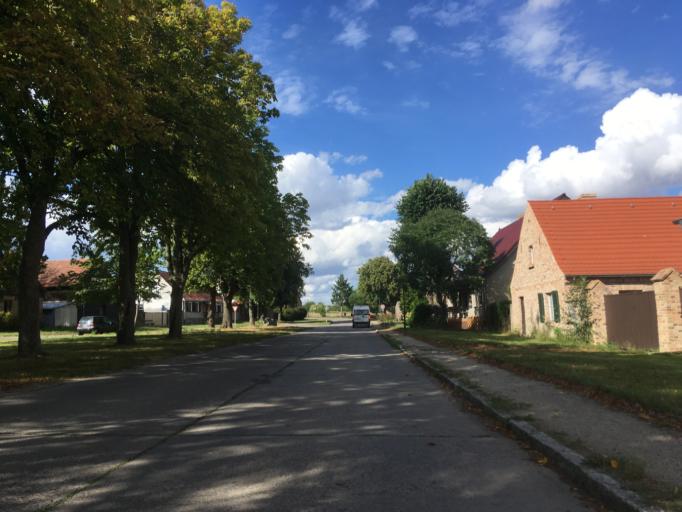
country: DE
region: Brandenburg
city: Liepe
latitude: 52.9137
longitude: 13.9623
